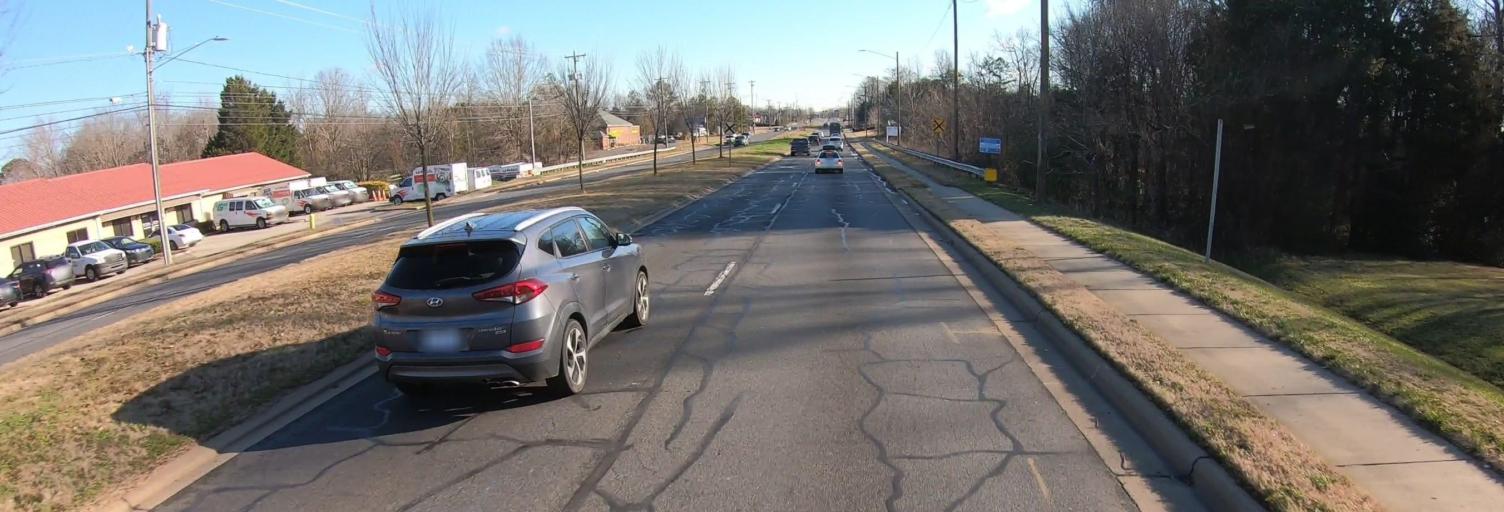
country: US
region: North Carolina
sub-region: Mecklenburg County
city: Pineville
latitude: 35.1190
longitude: -80.9544
